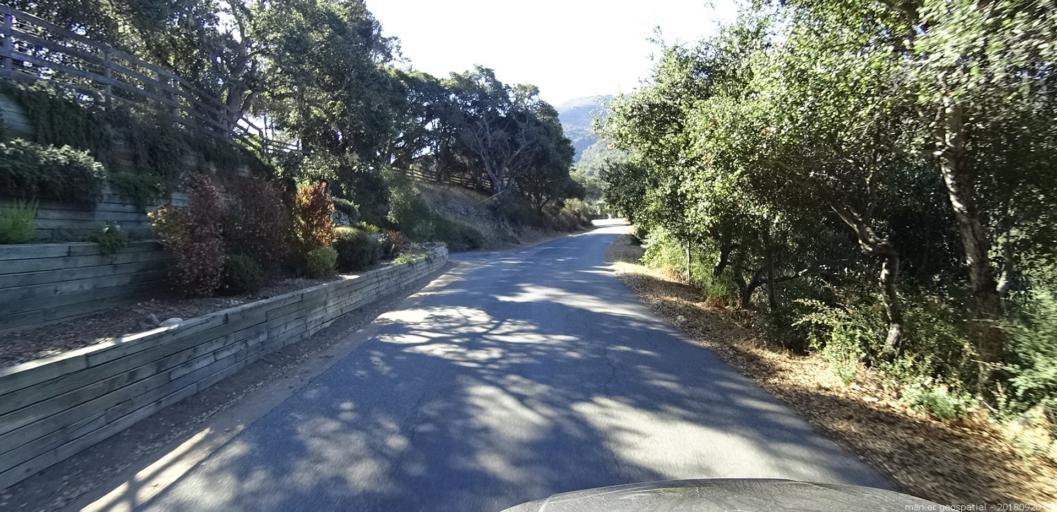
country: US
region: California
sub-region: Monterey County
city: Carmel Valley Village
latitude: 36.5197
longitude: -121.7894
